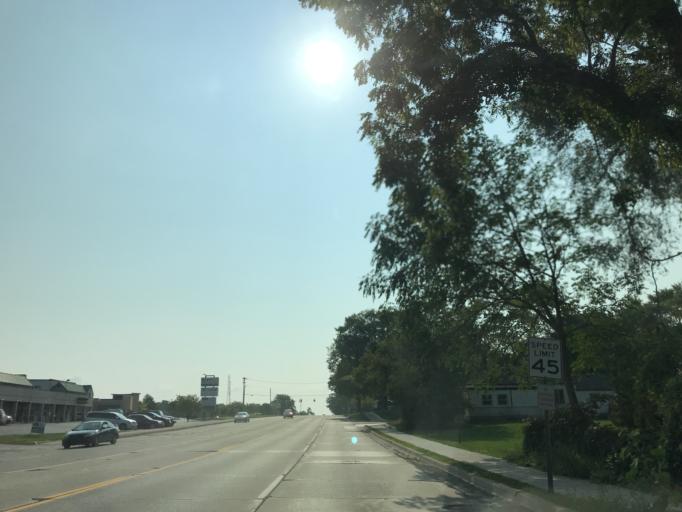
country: US
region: Michigan
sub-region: Washtenaw County
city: Ypsilanti
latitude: 42.2521
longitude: -83.6714
